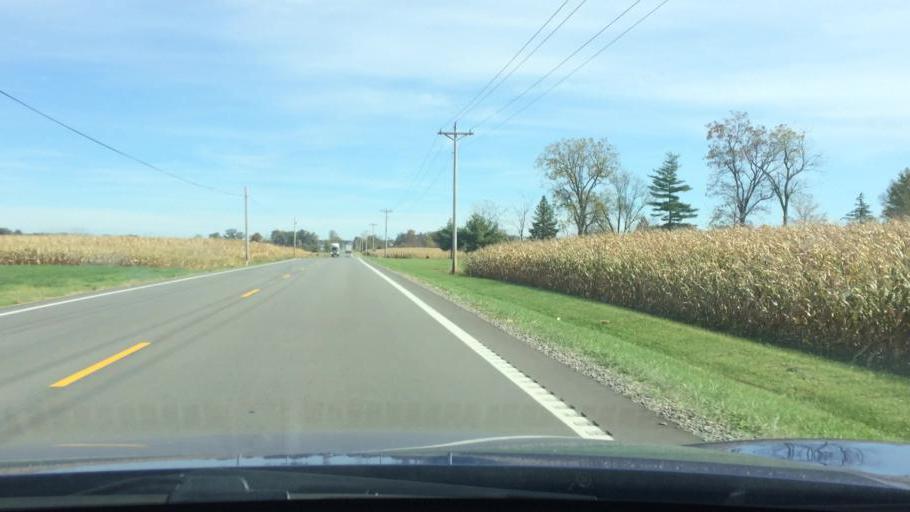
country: US
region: Ohio
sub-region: Logan County
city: Russells Point
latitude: 40.4433
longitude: -83.8455
